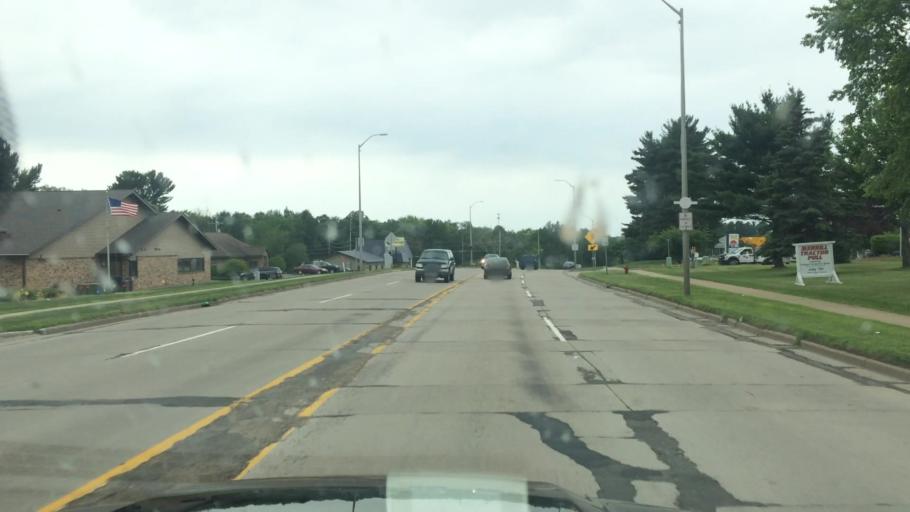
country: US
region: Wisconsin
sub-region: Lincoln County
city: Merrill
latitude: 45.1779
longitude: -89.6547
